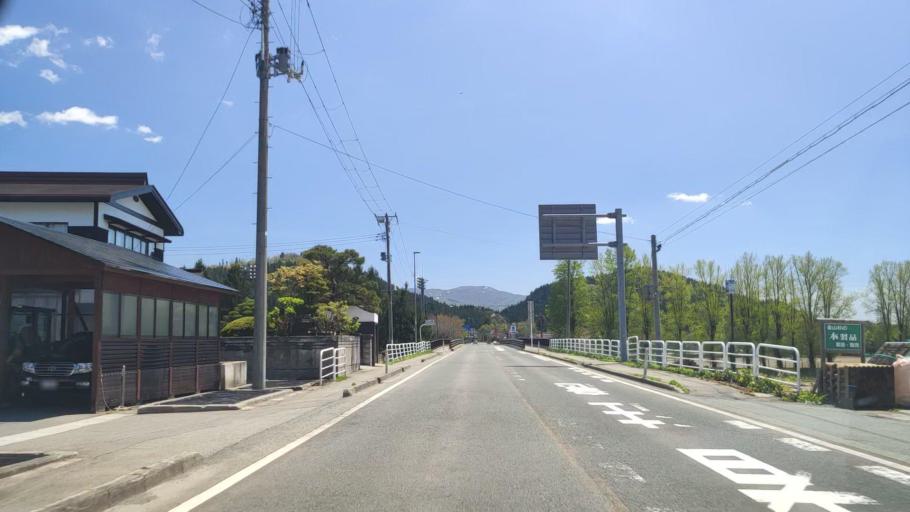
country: JP
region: Yamagata
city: Shinjo
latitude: 38.8862
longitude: 140.3340
